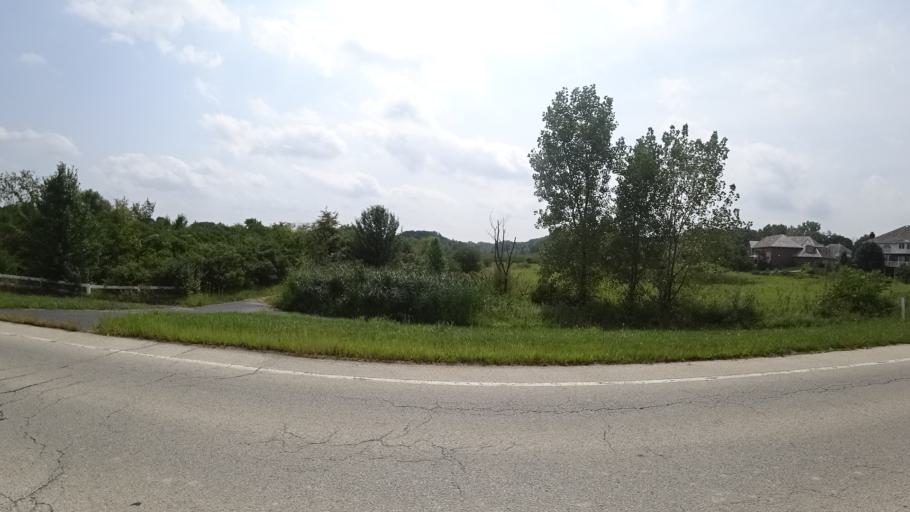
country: US
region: Illinois
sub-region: Will County
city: Goodings Grove
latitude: 41.6151
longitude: -87.8991
